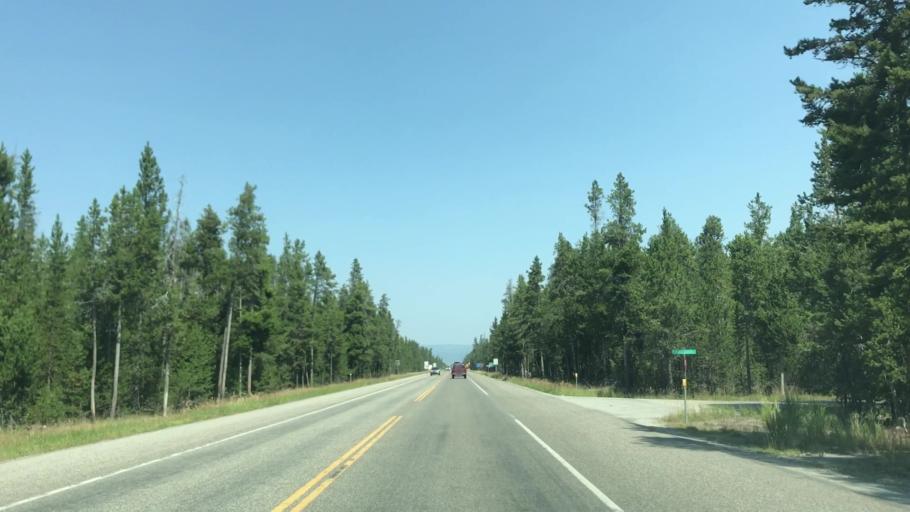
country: US
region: Montana
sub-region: Gallatin County
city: West Yellowstone
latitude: 44.6676
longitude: -111.1000
